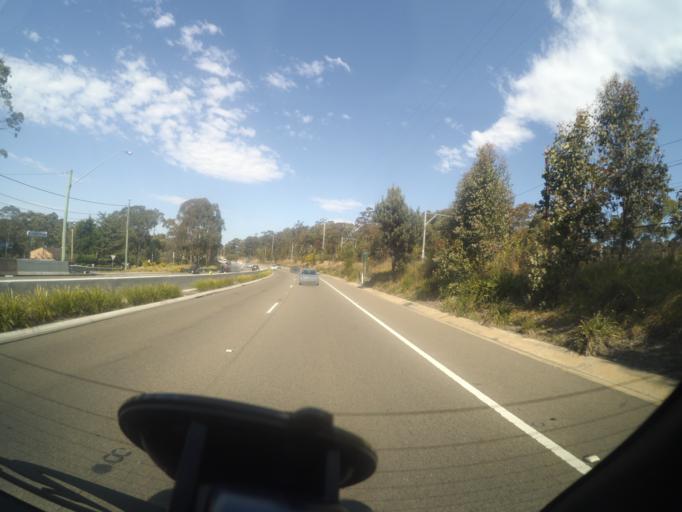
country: AU
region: New South Wales
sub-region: Blue Mountains Municipality
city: Blaxland
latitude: -33.7196
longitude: 150.5932
